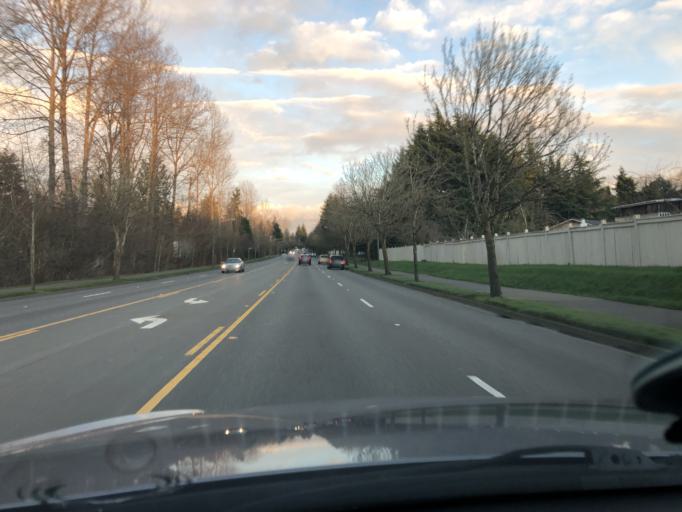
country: US
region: Washington
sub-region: King County
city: Federal Way
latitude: 47.3152
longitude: -122.3537
